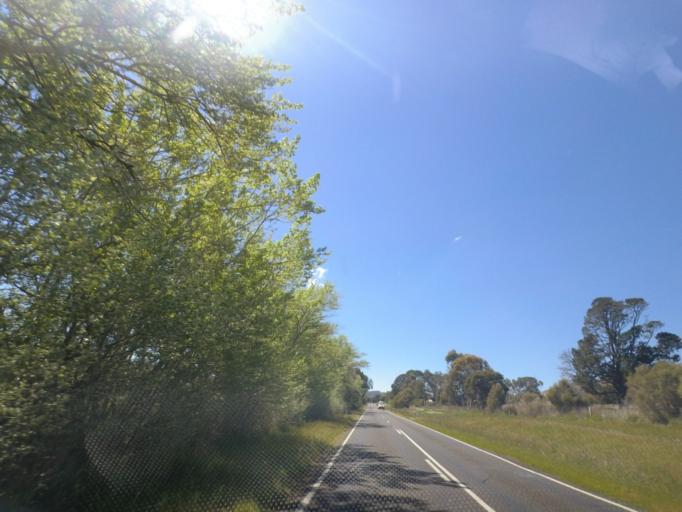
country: AU
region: Victoria
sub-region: Hume
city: Sunbury
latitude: -37.0976
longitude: 144.7594
